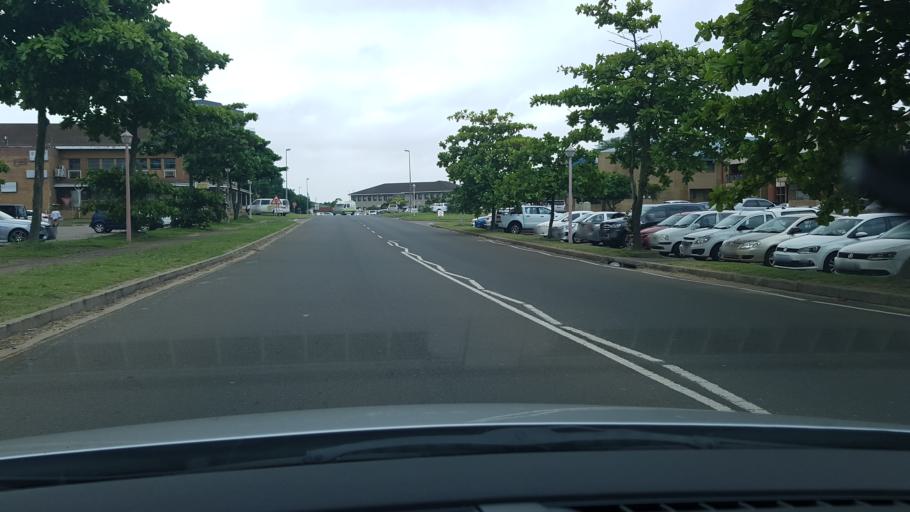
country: ZA
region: KwaZulu-Natal
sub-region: uThungulu District Municipality
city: Richards Bay
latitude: -28.7522
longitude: 32.0537
